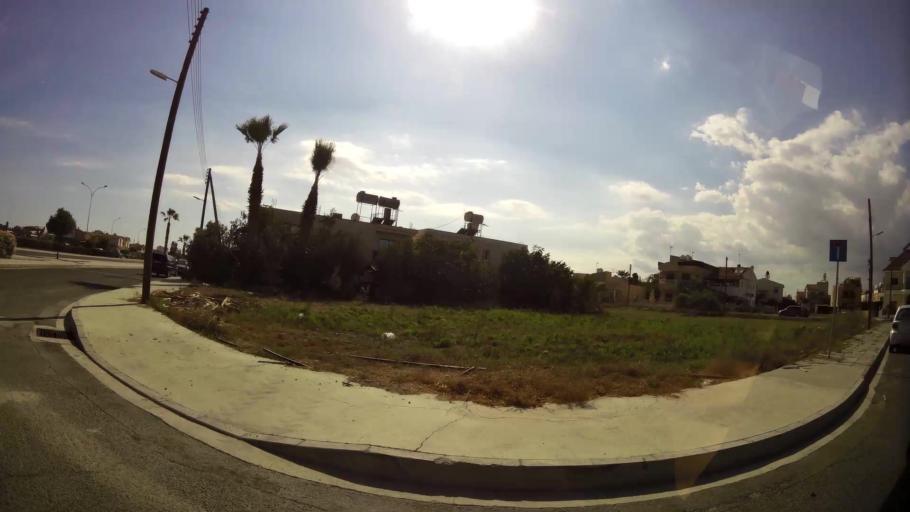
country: CY
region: Larnaka
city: Livadia
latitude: 34.9426
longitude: 33.6313
